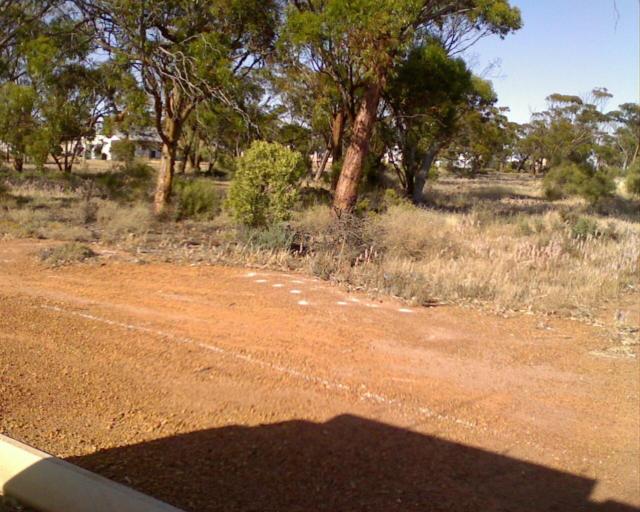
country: AU
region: Western Australia
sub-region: Merredin
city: Merredin
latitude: -31.1159
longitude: 117.7907
